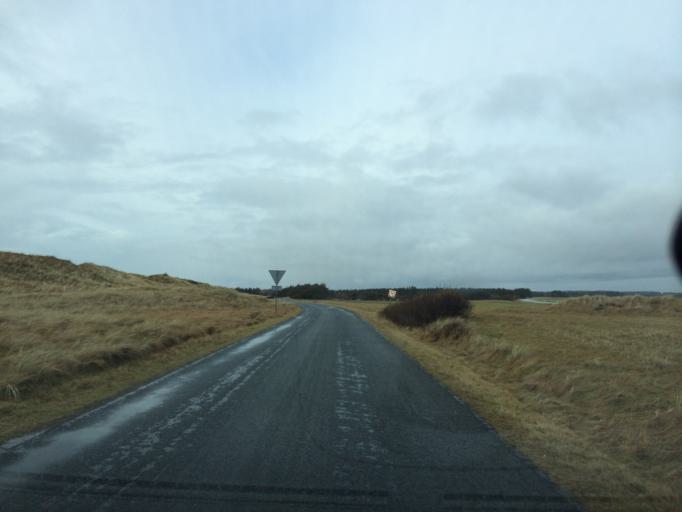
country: DK
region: Central Jutland
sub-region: Holstebro Kommune
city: Ulfborg
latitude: 56.2446
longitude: 8.1389
